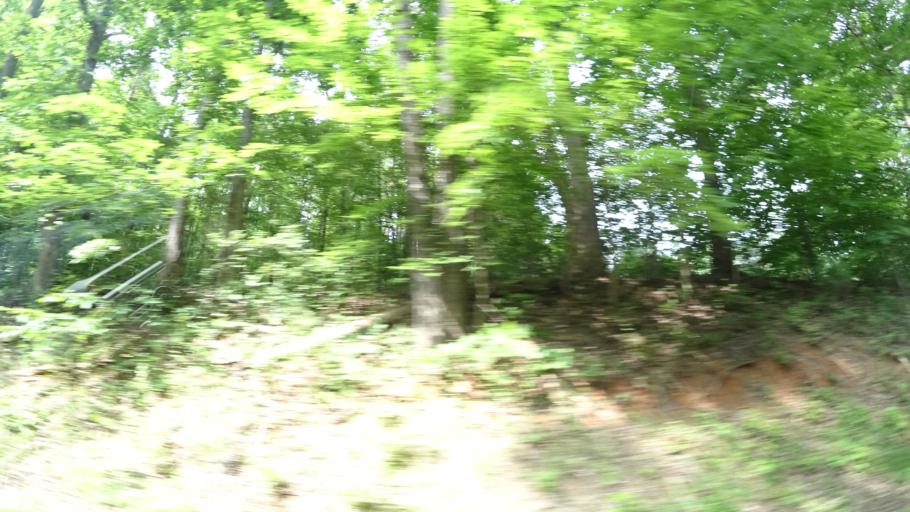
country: US
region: Virginia
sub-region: Spotsylvania County
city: Spotsylvania Courthouse
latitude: 38.1571
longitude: -77.6341
